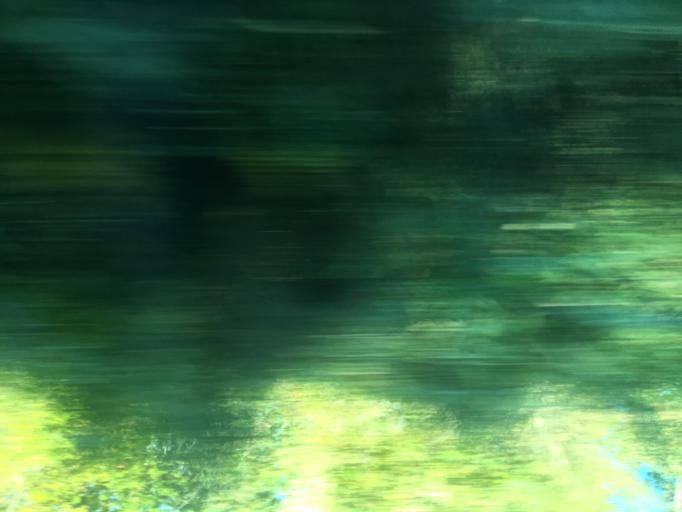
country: JP
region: Ibaraki
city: Kasama
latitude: 36.3663
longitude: 140.2565
